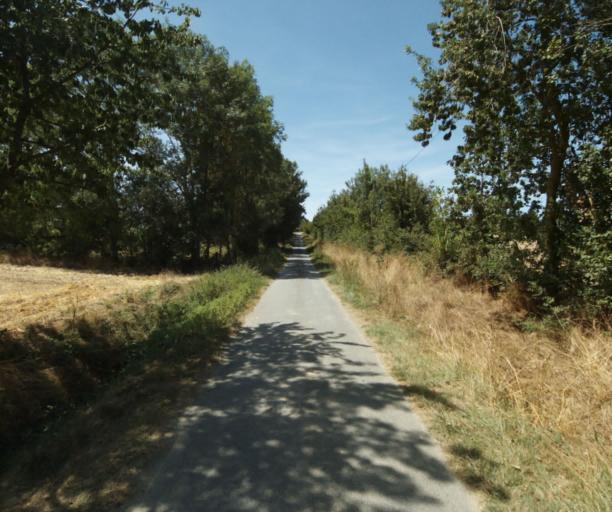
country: FR
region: Midi-Pyrenees
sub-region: Departement de la Haute-Garonne
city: Revel
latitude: 43.5033
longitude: 2.0354
